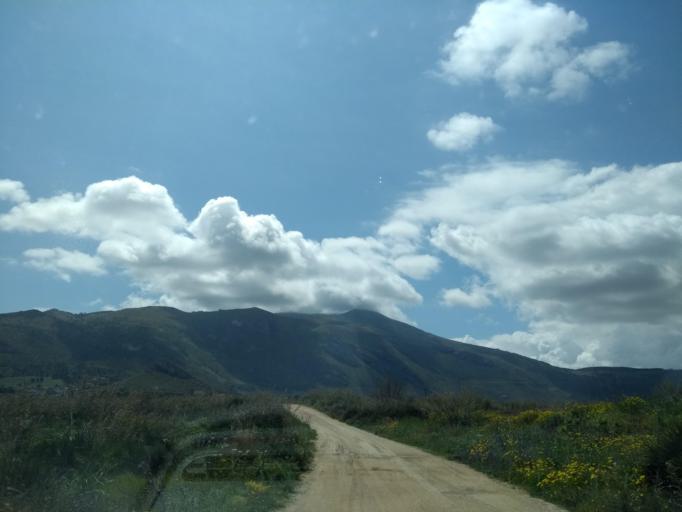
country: IT
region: Sicily
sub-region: Trapani
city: Castellammare del Golfo
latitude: 38.0481
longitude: 12.8477
